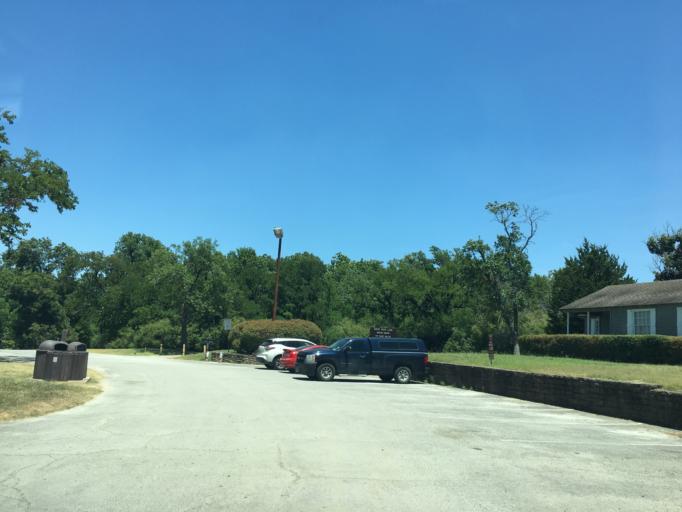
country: US
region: Texas
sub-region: Dallas County
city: Highland Park
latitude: 32.8330
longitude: -96.7116
